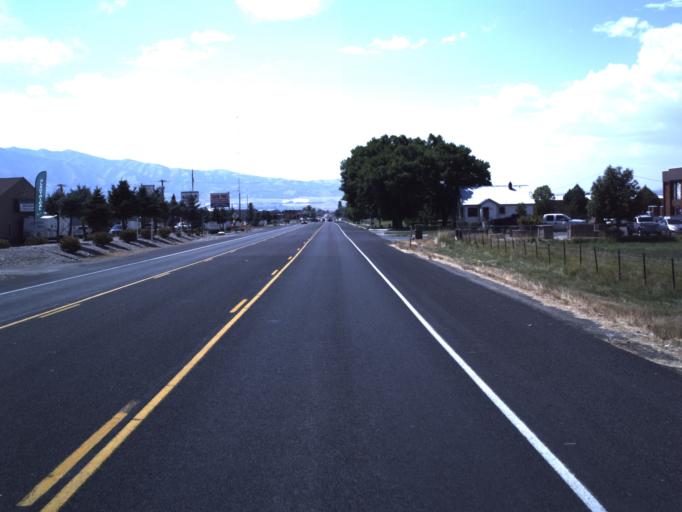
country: US
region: Utah
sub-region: Cache County
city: Logan
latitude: 41.7356
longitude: -111.8519
